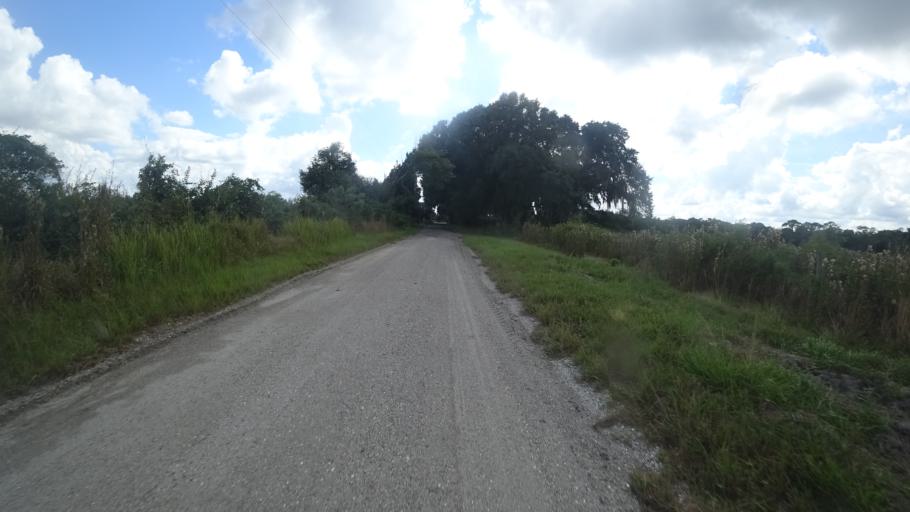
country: US
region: Florida
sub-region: Hillsborough County
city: Wimauma
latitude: 27.5419
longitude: -82.1746
